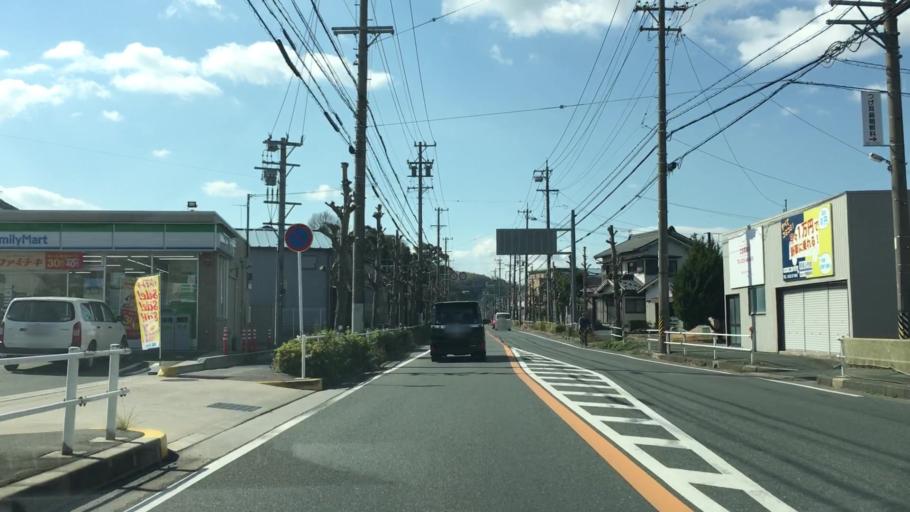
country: JP
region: Aichi
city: Gamagori
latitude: 34.8245
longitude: 137.2151
